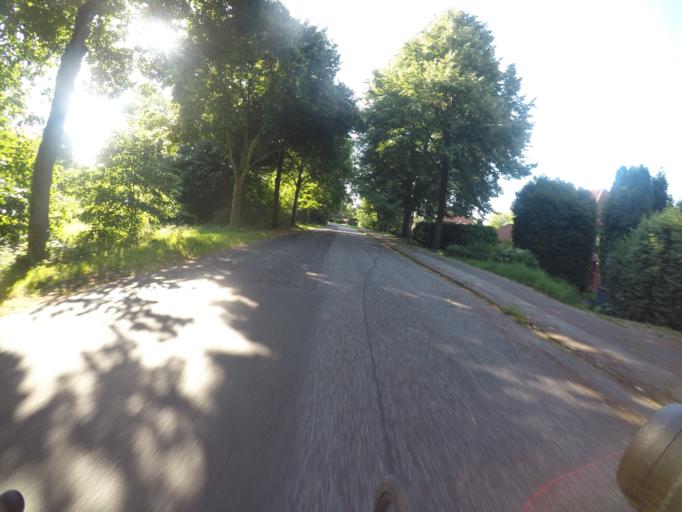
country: DE
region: Hamburg
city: Bergedorf
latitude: 53.4861
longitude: 10.1902
